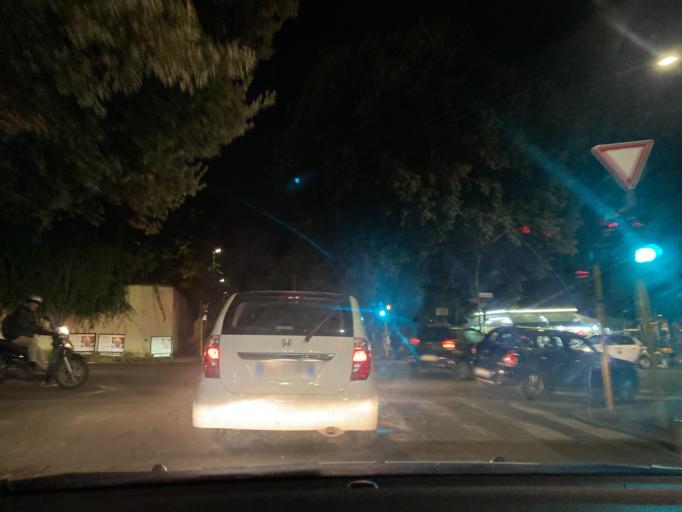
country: VA
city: Vatican City
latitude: 41.9196
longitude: 12.4788
